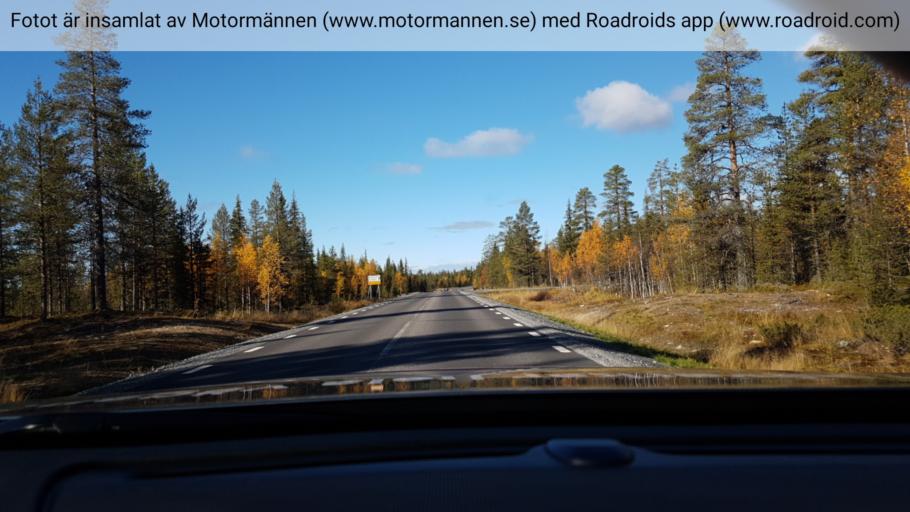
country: SE
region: Norrbotten
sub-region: Gallivare Kommun
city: Gaellivare
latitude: 66.9444
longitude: 20.8069
